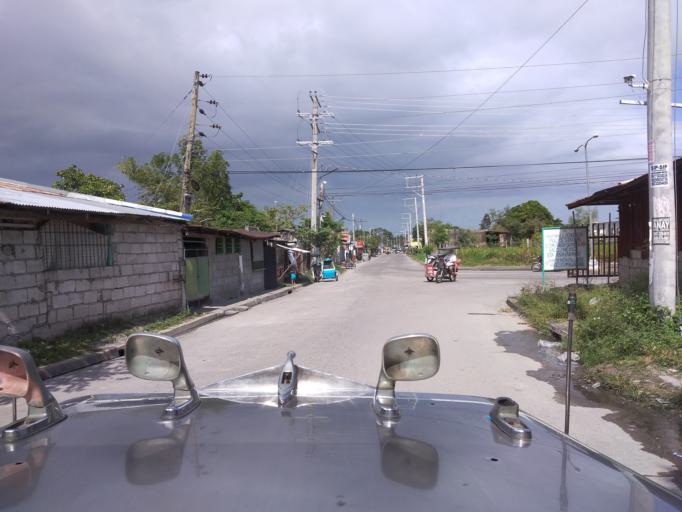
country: PH
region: Central Luzon
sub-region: Province of Pampanga
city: Pandacaqui
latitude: 15.1812
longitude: 120.6415
